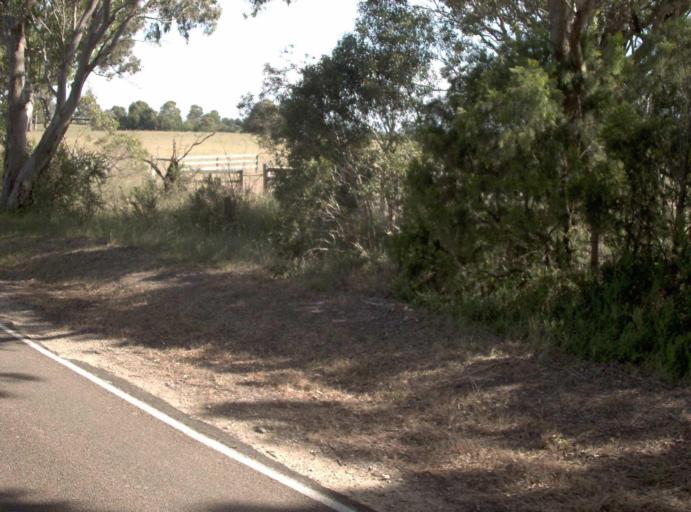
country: AU
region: Victoria
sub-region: East Gippsland
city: Lakes Entrance
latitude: -37.8156
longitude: 147.8500
